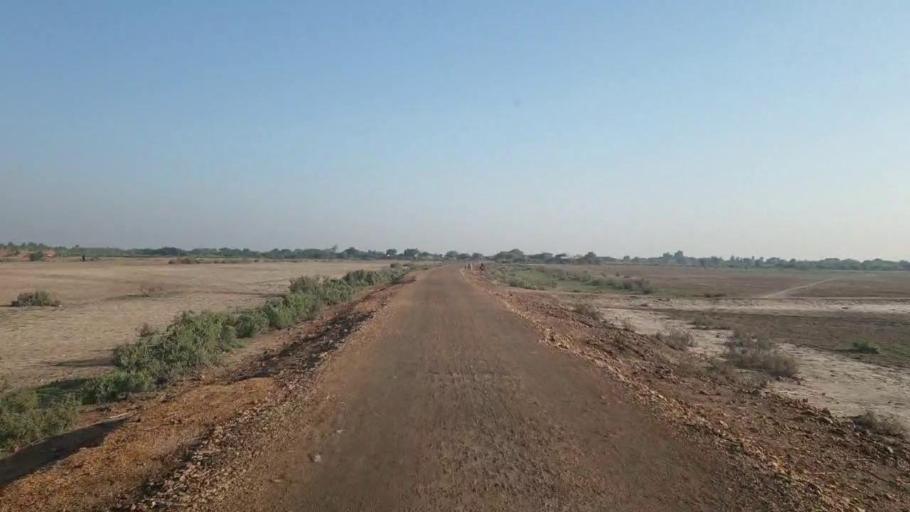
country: PK
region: Sindh
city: Badin
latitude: 24.7271
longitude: 68.8652
